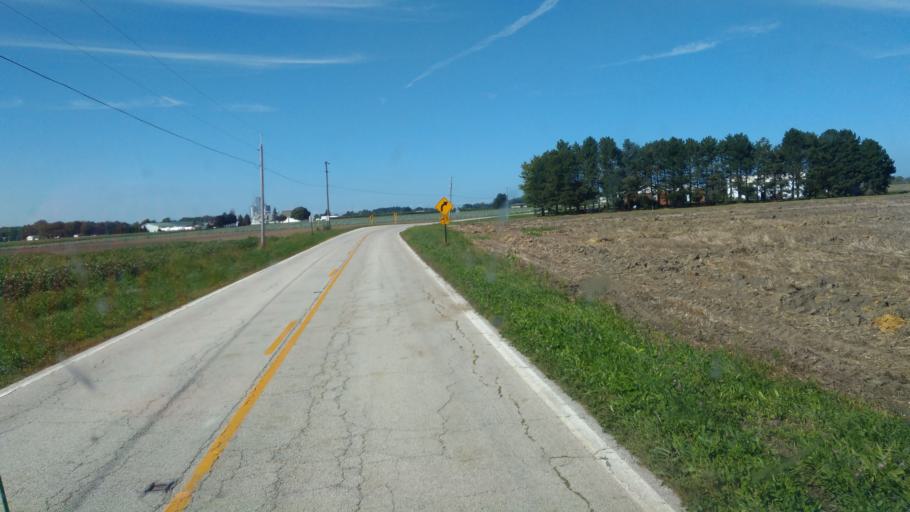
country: US
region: Ohio
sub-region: Ottawa County
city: Port Clinton
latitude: 41.4101
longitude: -82.8936
